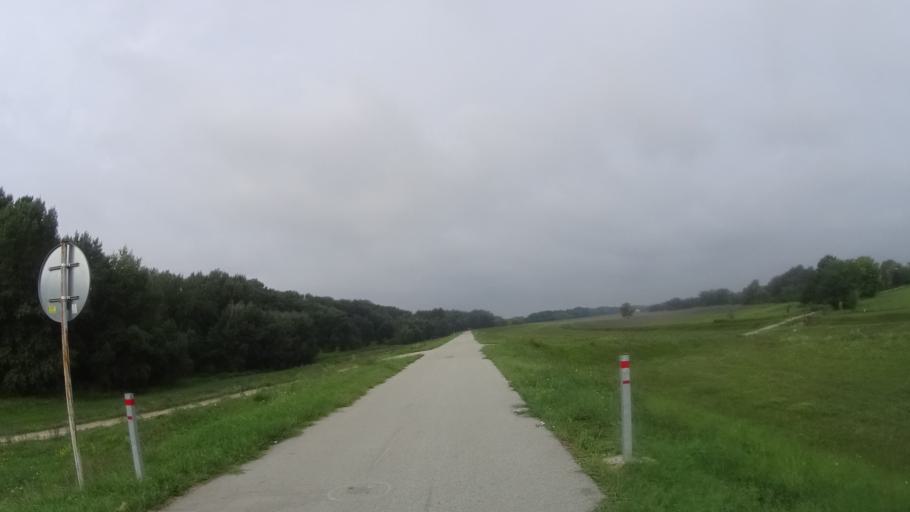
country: SK
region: Nitriansky
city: Komarno
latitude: 47.7441
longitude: 18.1806
